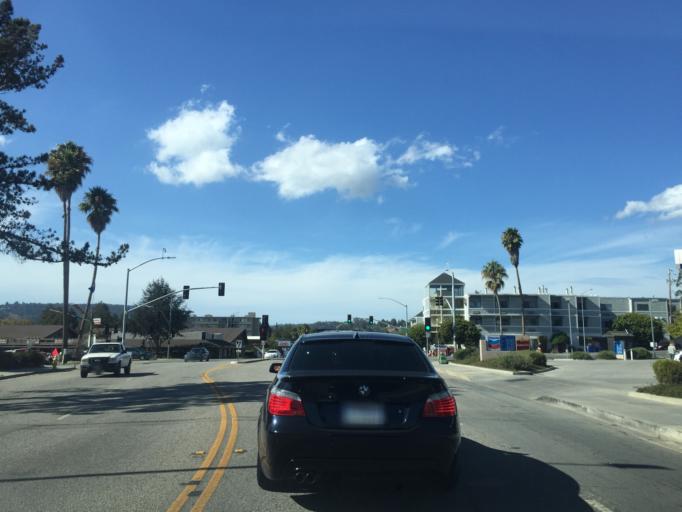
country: US
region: California
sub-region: Santa Cruz County
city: Santa Cruz
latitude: 36.9740
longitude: -122.0186
